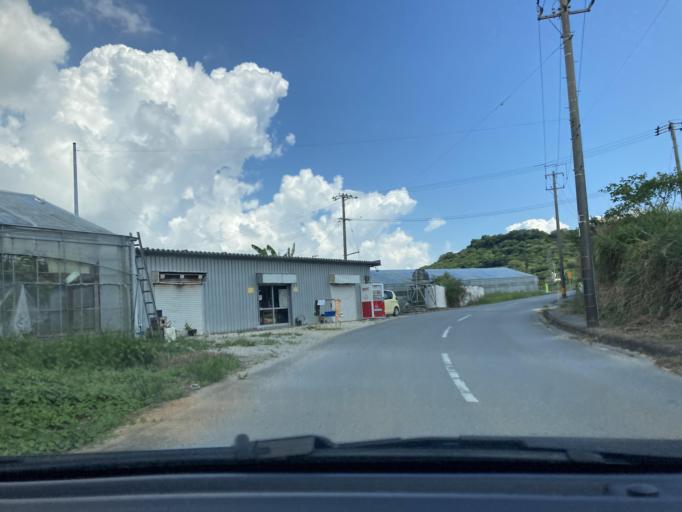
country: JP
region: Okinawa
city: Tomigusuku
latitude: 26.1594
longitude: 127.7551
